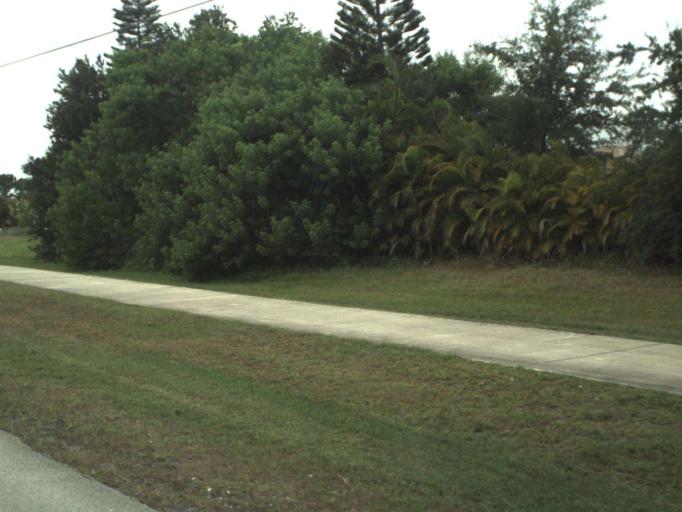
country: US
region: Florida
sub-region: Saint Lucie County
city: River Park
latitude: 27.3399
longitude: -80.3506
